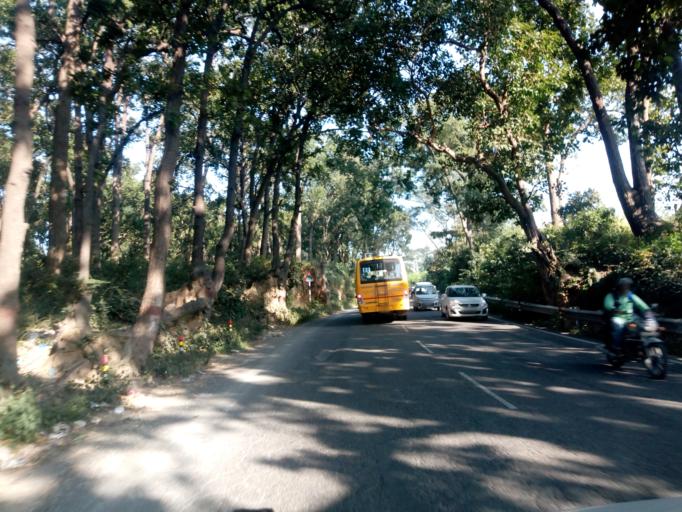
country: IN
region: Uttarakhand
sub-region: Dehradun
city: Vikasnagar
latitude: 30.3470
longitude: 77.8742
